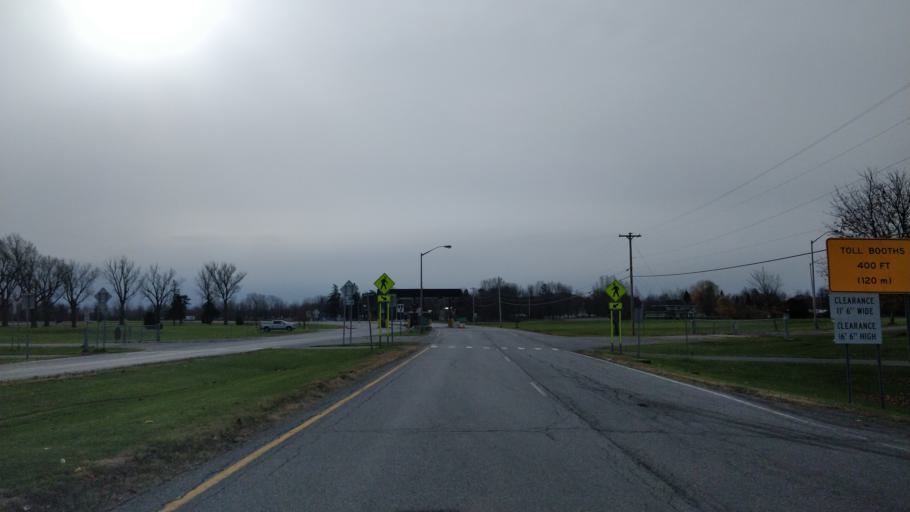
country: US
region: New York
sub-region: St. Lawrence County
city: Ogdensburg
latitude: 44.7196
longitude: -75.4542
